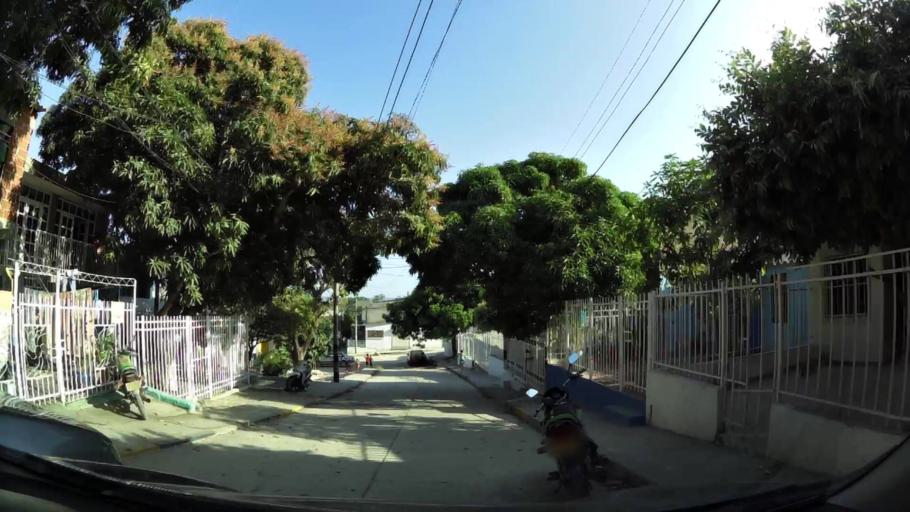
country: CO
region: Bolivar
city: Cartagena
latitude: 10.4021
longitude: -75.4798
